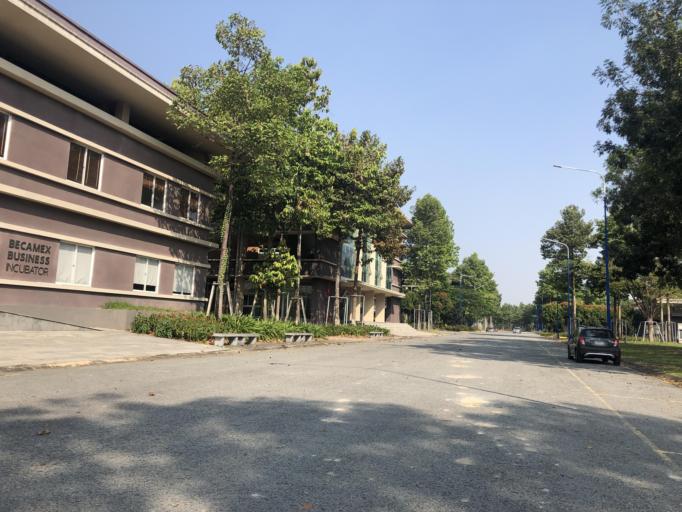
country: VN
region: Binh Duong
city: Thu Dau Mot
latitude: 11.0520
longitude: 106.6682
